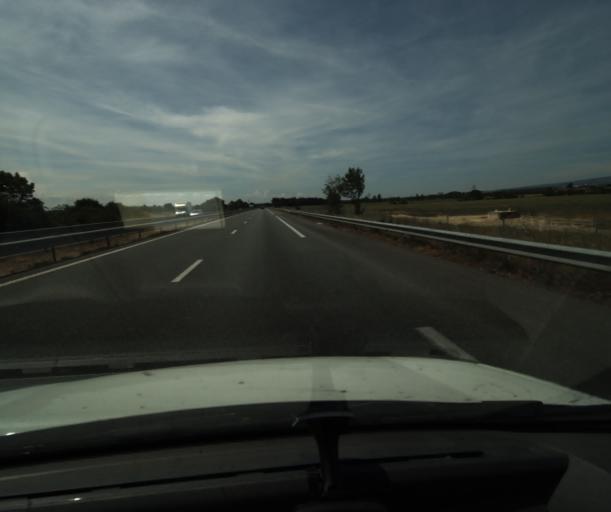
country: FR
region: Languedoc-Roussillon
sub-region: Departement de l'Aude
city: Alzonne
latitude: 43.2232
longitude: 2.1680
